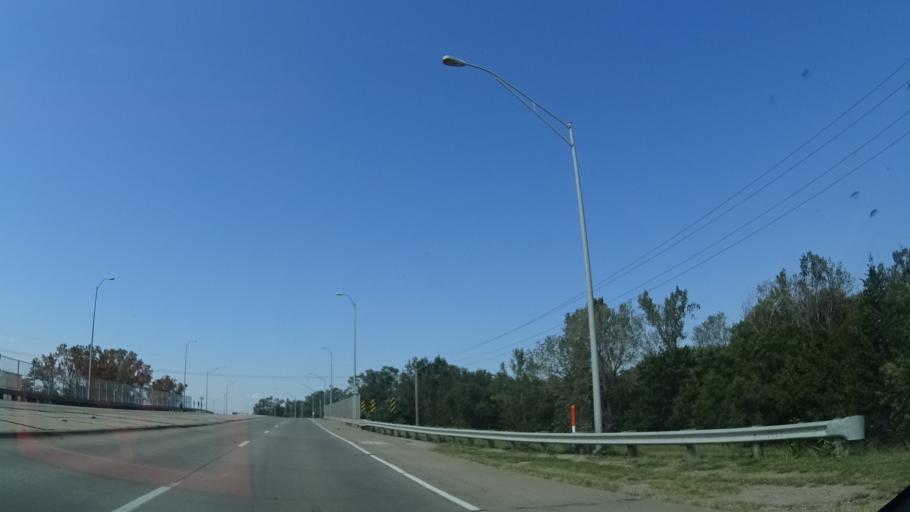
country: US
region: Nebraska
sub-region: Sarpy County
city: Offutt Air Force Base
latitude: 41.1160
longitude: -95.9289
